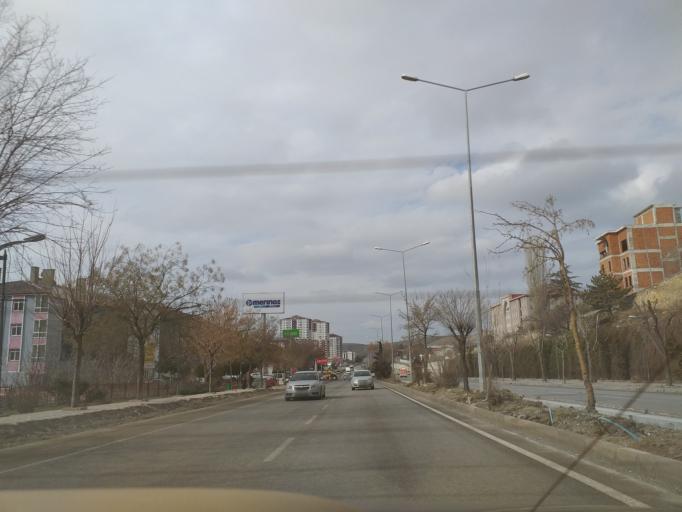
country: TR
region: Yozgat
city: Yozgat
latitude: 39.8191
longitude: 34.7999
